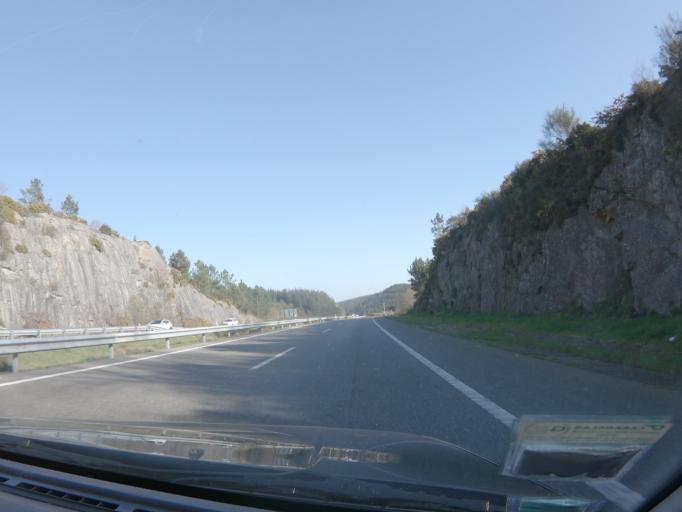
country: ES
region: Galicia
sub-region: Provincia de Lugo
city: Guitiriz
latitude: 43.1775
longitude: -7.8029
